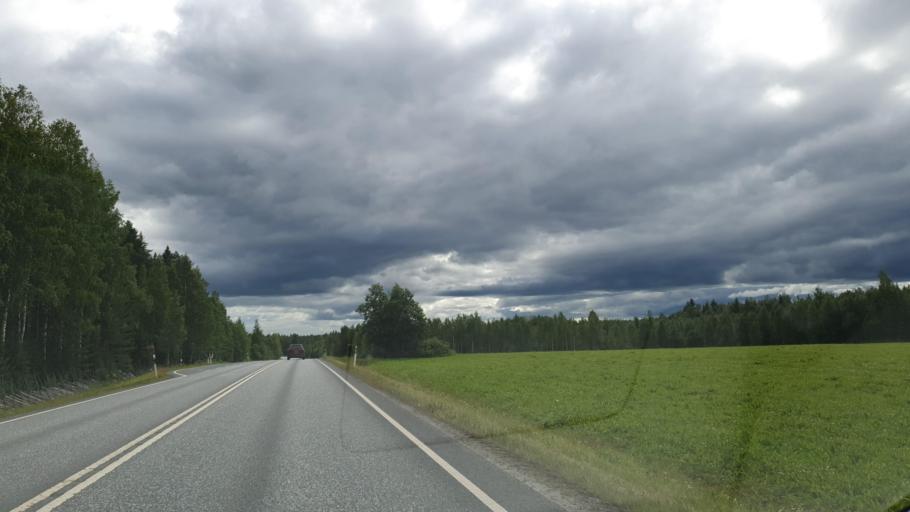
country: FI
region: Northern Savo
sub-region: Ylae-Savo
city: Sonkajaervi
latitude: 63.8094
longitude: 27.4190
